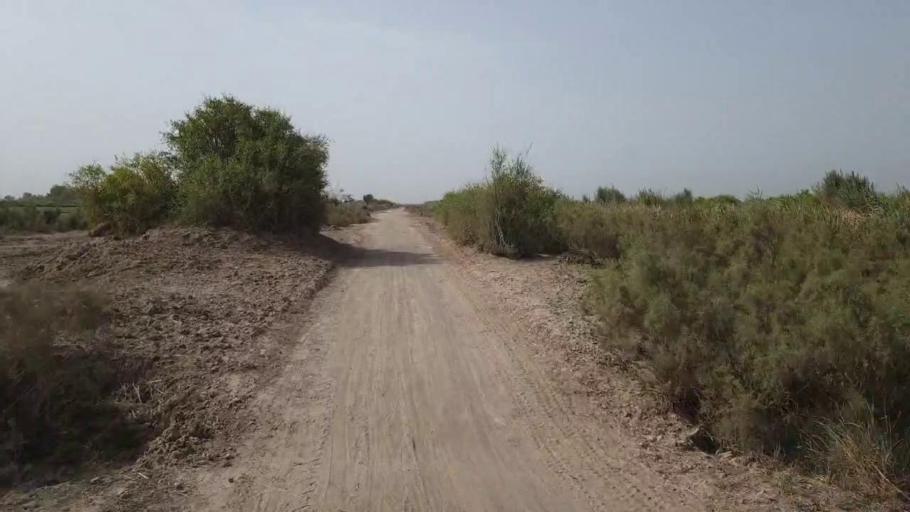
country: PK
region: Sindh
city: Daur
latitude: 26.4128
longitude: 68.1609
